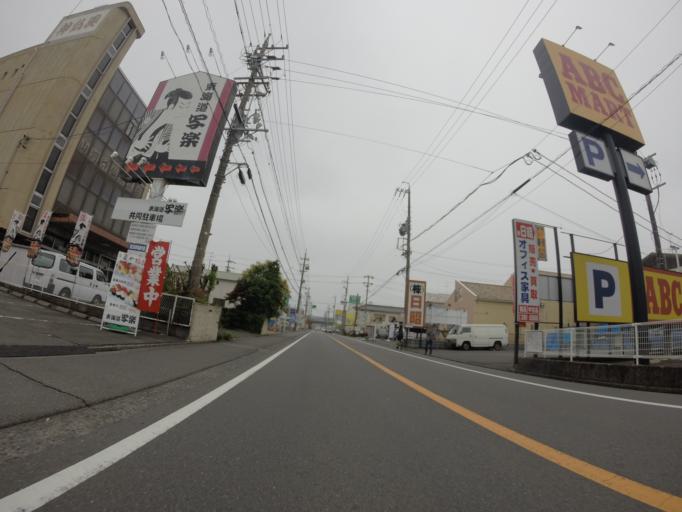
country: JP
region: Shizuoka
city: Shizuoka-shi
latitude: 34.9506
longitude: 138.3964
